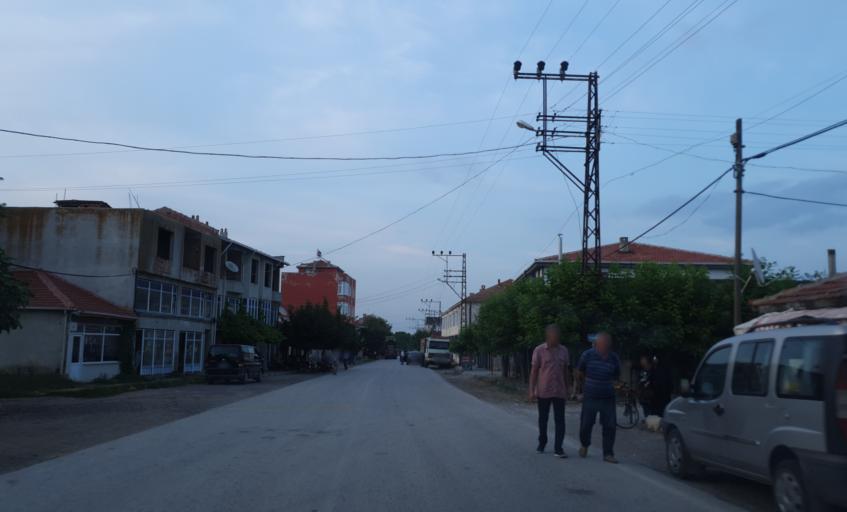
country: TR
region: Tekirdag
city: Beyazkoy
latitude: 41.3848
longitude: 27.6200
